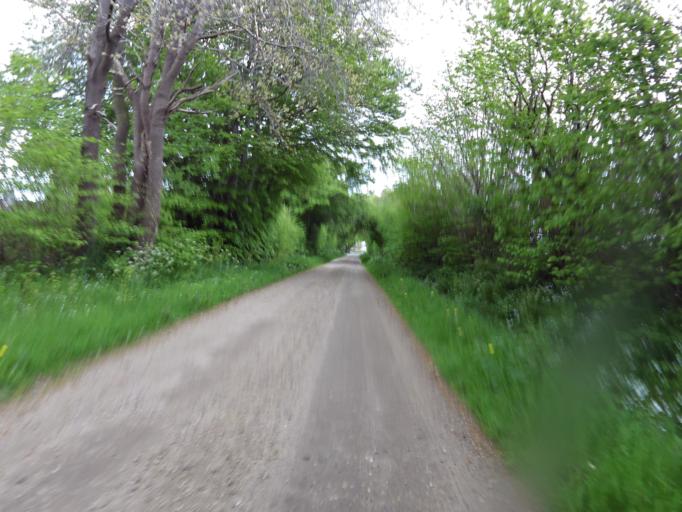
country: DK
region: South Denmark
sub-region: Haderslev Kommune
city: Gram
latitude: 55.2846
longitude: 9.0338
